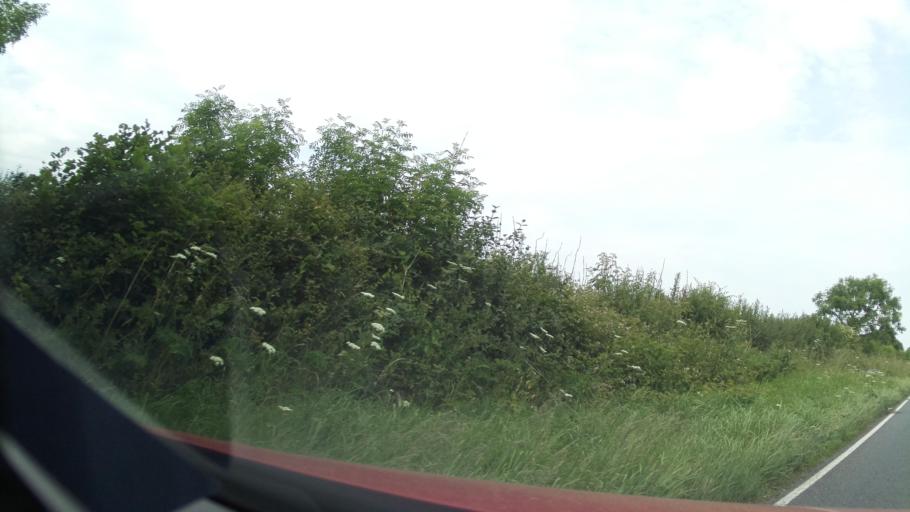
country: GB
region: England
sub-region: Devon
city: Sidmouth
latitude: 50.7026
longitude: -3.1857
